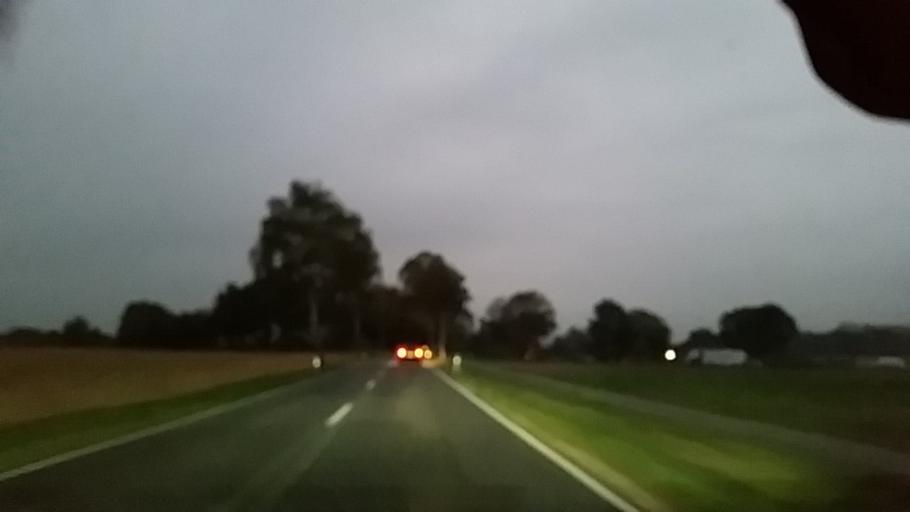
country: DE
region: Lower Saxony
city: Wieren
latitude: 52.8806
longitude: 10.6638
